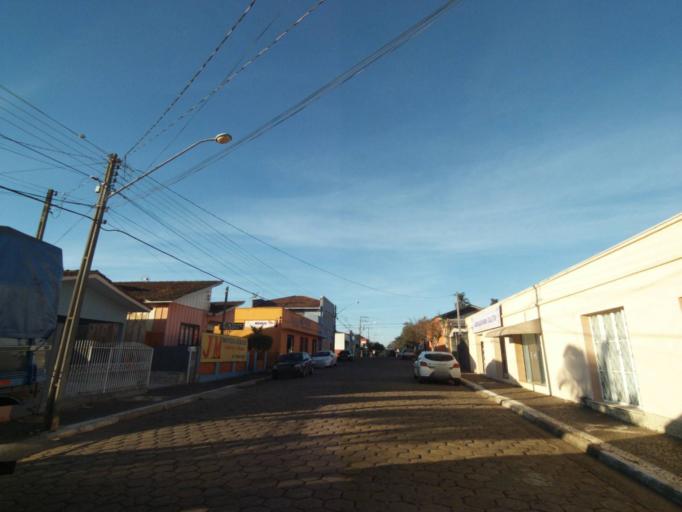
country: BR
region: Parana
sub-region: Tibagi
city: Tibagi
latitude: -24.5150
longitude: -50.4117
